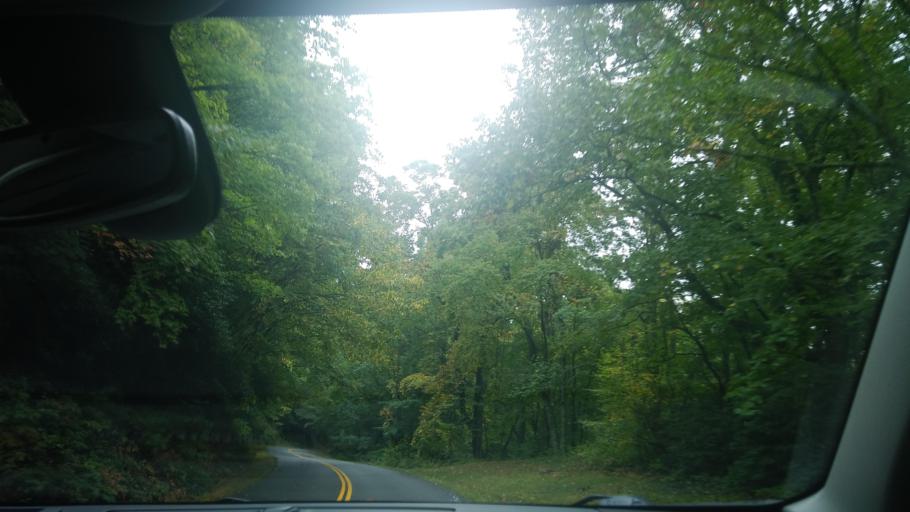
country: US
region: North Carolina
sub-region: Mitchell County
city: Spruce Pine
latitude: 35.9071
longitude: -81.9721
